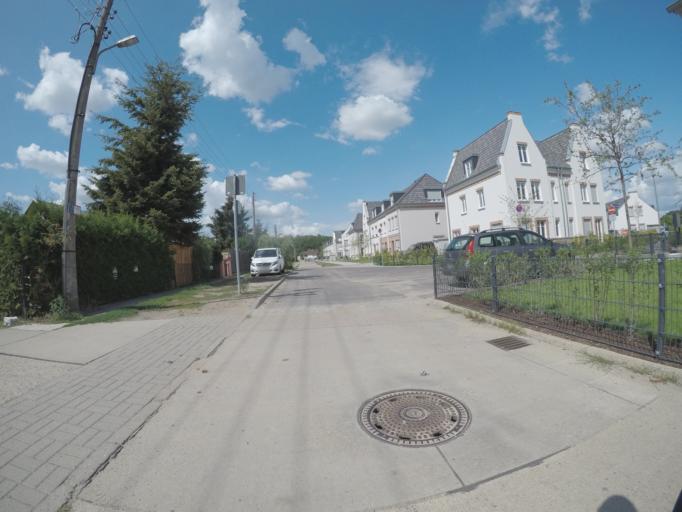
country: DE
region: Berlin
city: Kaulsdorf
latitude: 52.5023
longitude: 13.5760
